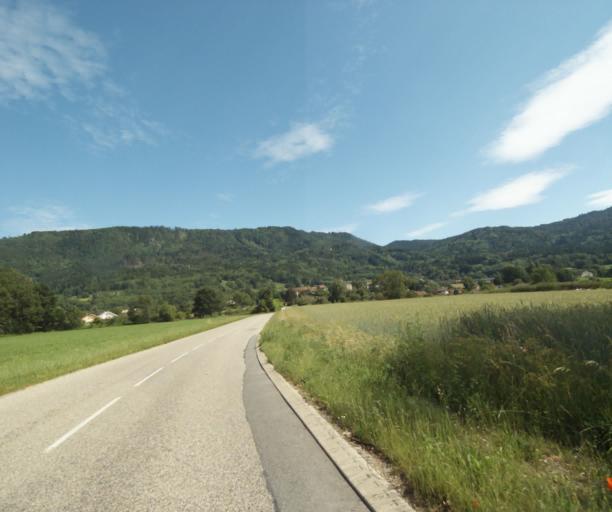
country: FR
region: Rhone-Alpes
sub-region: Departement de la Haute-Savoie
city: Perrignier
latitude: 46.2897
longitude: 6.4377
